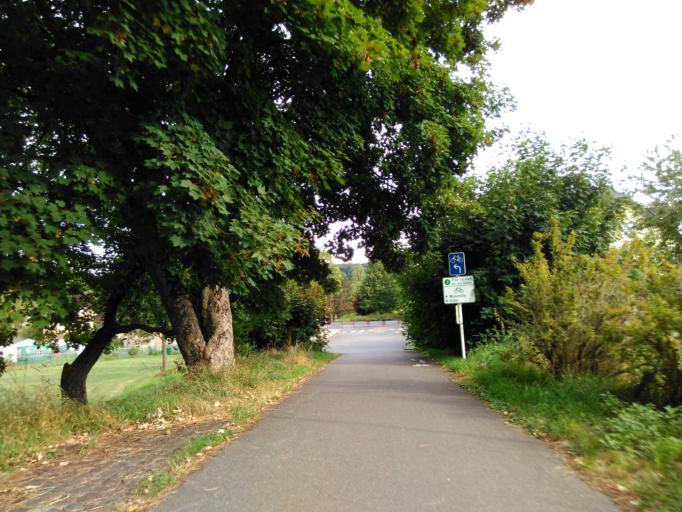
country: LU
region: Grevenmacher
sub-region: Canton d'Echternach
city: Rosport
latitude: 49.8065
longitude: 6.5060
